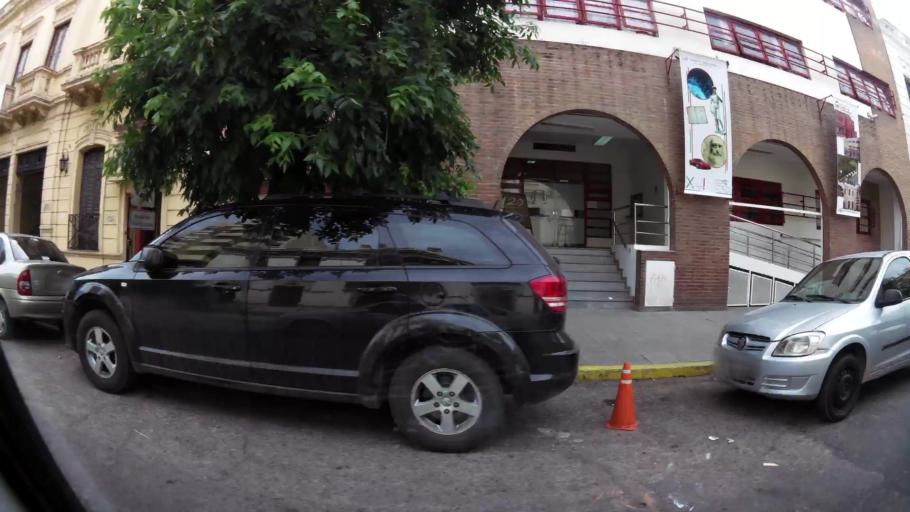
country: AR
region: Buenos Aires
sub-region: Partido de La Plata
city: La Plata
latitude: -34.9205
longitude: -57.9501
